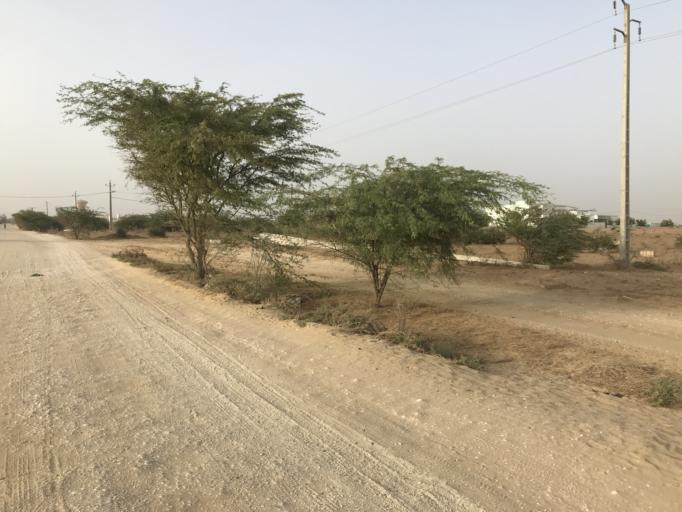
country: SN
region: Saint-Louis
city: Saint-Louis
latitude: 16.0276
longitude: -16.4454
